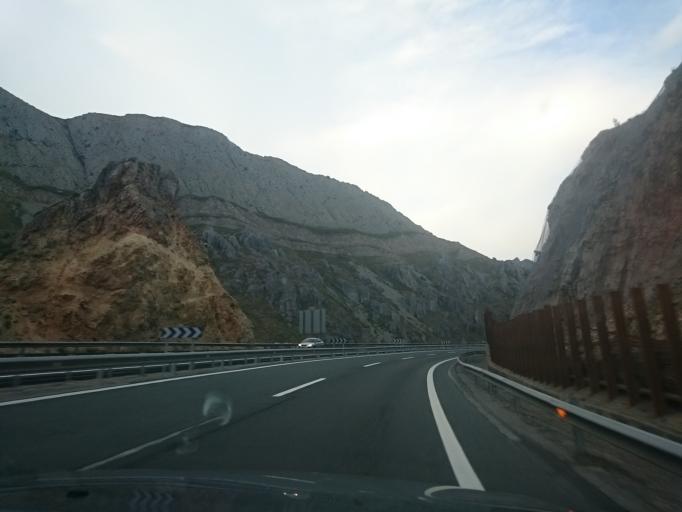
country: ES
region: Castille and Leon
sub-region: Provincia de Leon
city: Sena de Luna
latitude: 42.9331
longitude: -5.8510
